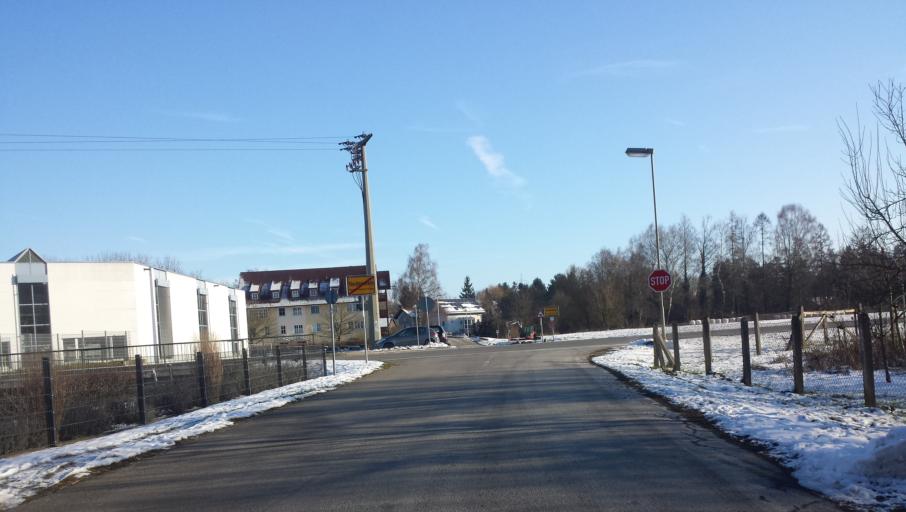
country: DE
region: Baden-Wuerttemberg
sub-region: Karlsruhe Region
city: Neidenstein
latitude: 49.3152
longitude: 8.8892
